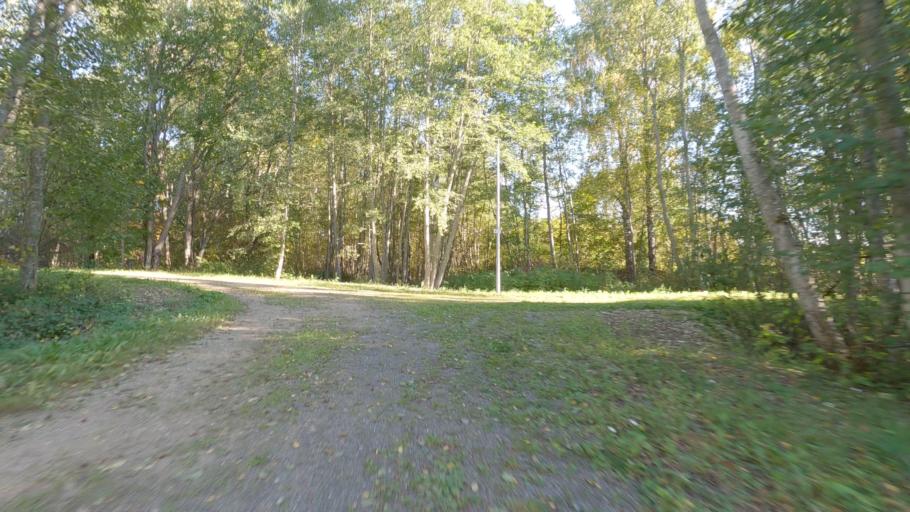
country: EE
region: Raplamaa
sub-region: Rapla vald
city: Rapla
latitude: 58.9977
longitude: 24.8214
